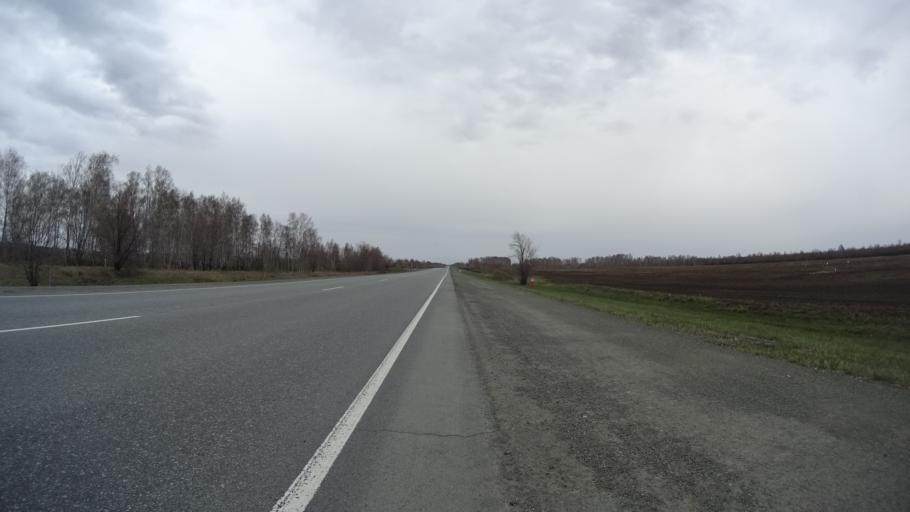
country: RU
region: Chelyabinsk
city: Krasnogorskiy
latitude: 54.6595
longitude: 61.2555
